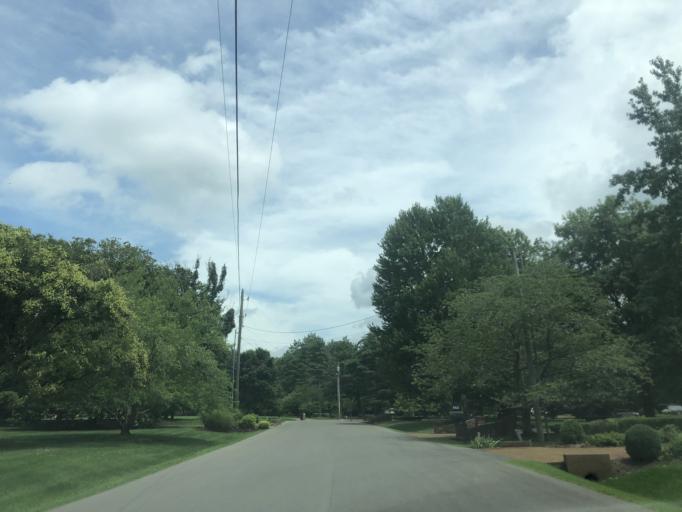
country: US
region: Tennessee
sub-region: Davidson County
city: Forest Hills
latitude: 36.0629
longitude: -86.8195
